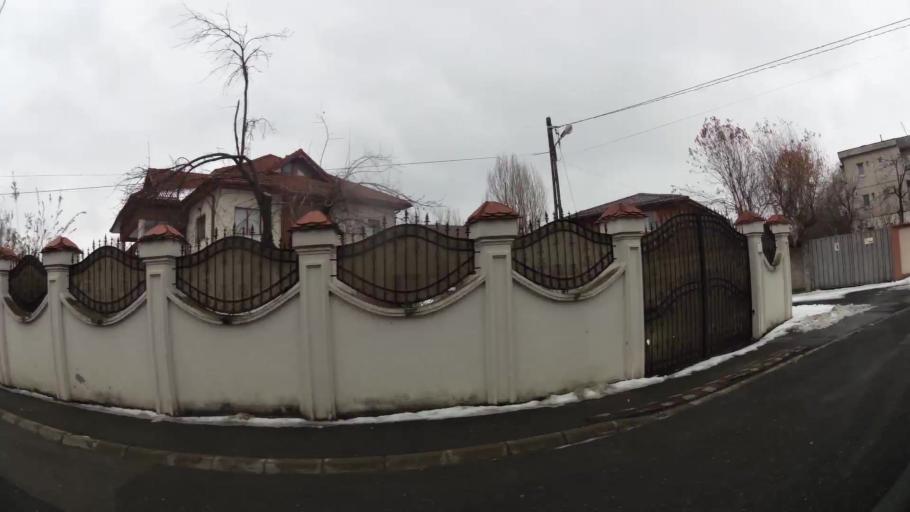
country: RO
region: Ilfov
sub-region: Comuna Otopeni
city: Otopeni
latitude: 44.5485
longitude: 26.0756
